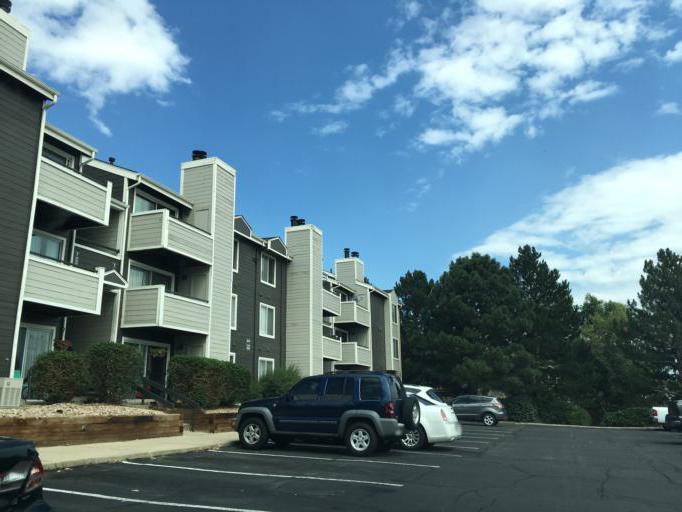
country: US
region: Colorado
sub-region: Jefferson County
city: Applewood
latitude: 39.7441
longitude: -105.1213
